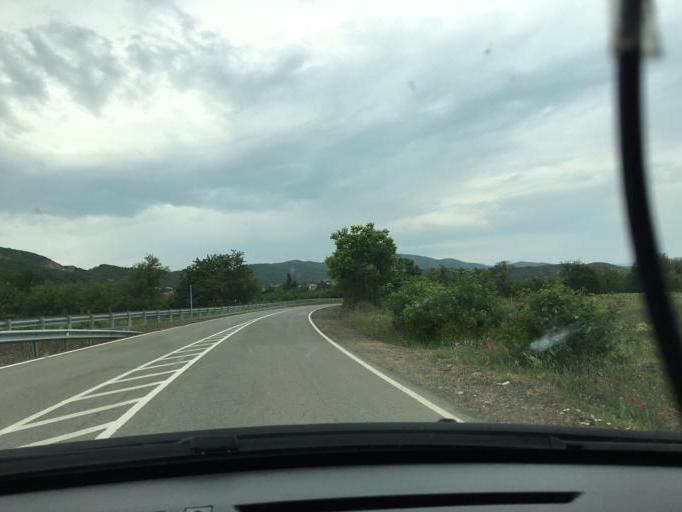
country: MK
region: Gevgelija
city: Miravci
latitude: 41.3027
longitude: 22.4424
